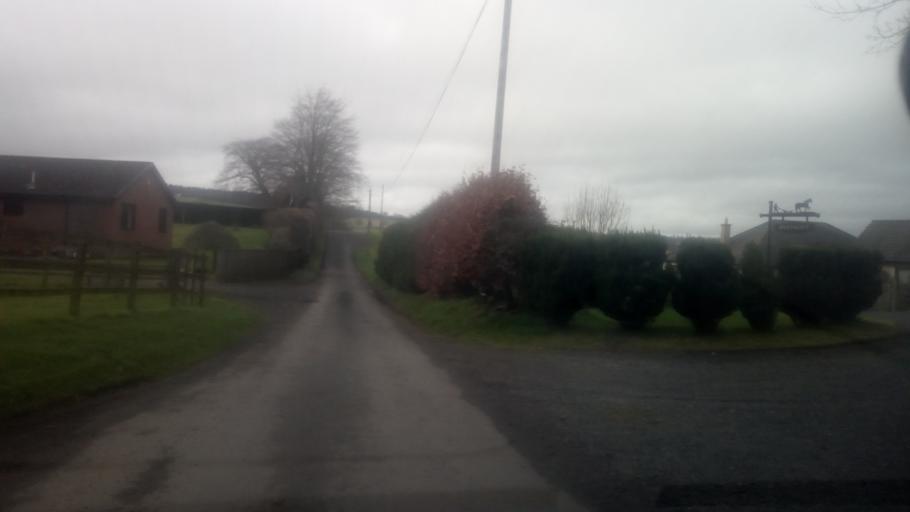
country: GB
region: Scotland
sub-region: The Scottish Borders
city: Jedburgh
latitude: 55.4862
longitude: -2.5368
